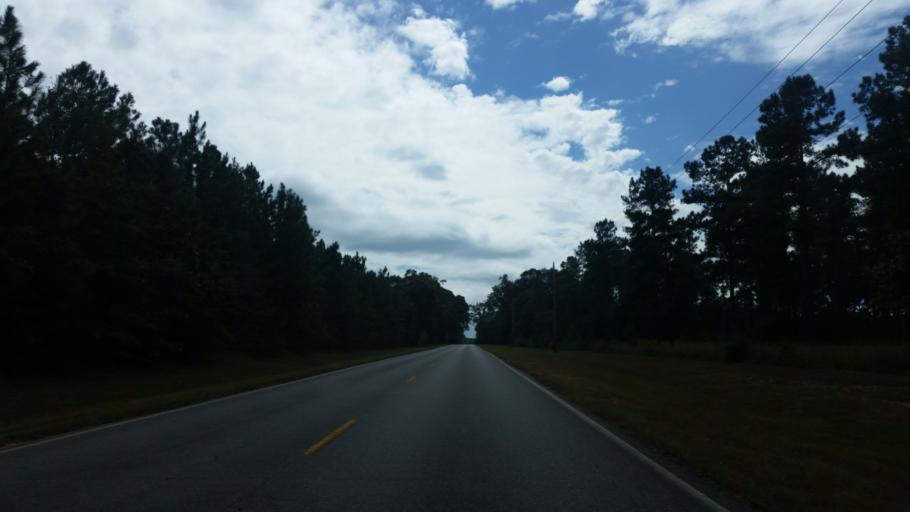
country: US
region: Florida
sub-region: Santa Rosa County
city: Point Baker
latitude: 30.7845
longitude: -86.9405
